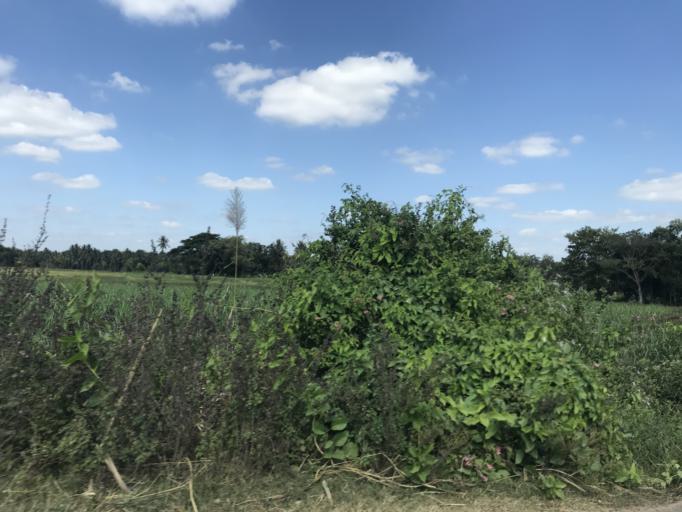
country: IN
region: Karnataka
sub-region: Mandya
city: Krishnarajpet
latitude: 12.5924
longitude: 76.3555
